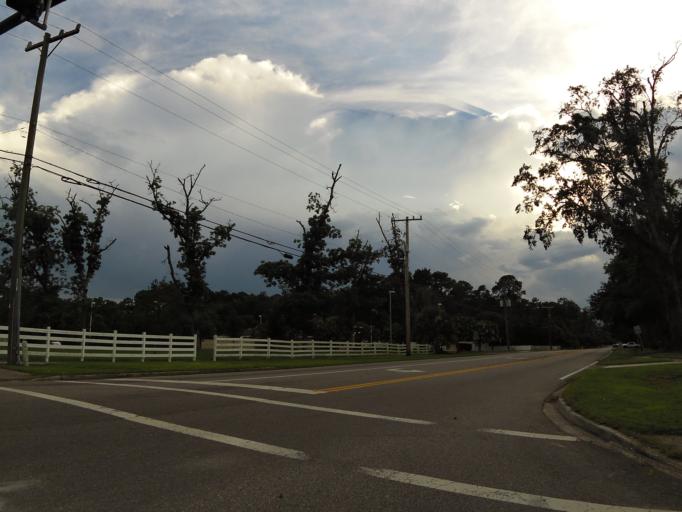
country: US
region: Florida
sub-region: Clay County
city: Bellair-Meadowbrook Terrace
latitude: 30.3005
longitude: -81.7838
